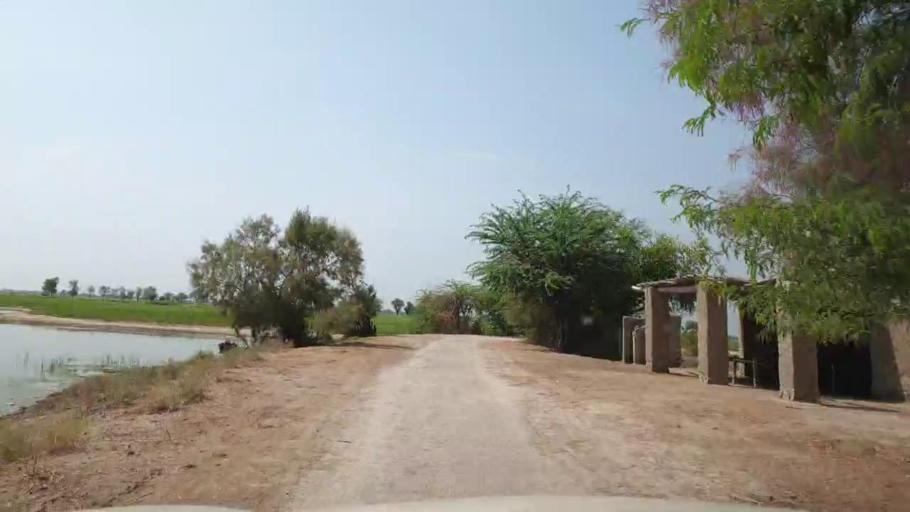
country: PK
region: Sindh
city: Ratodero
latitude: 27.8384
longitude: 68.2647
